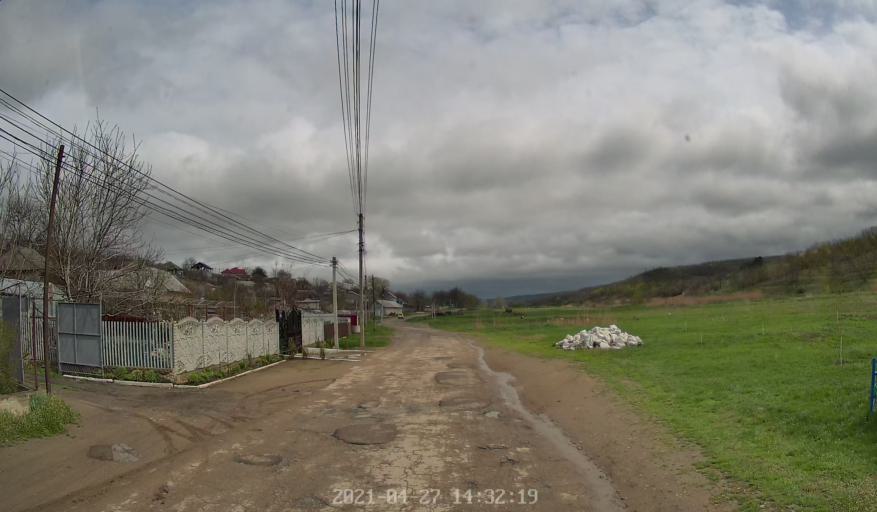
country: MD
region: Chisinau
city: Vadul lui Voda
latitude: 47.0629
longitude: 29.0120
